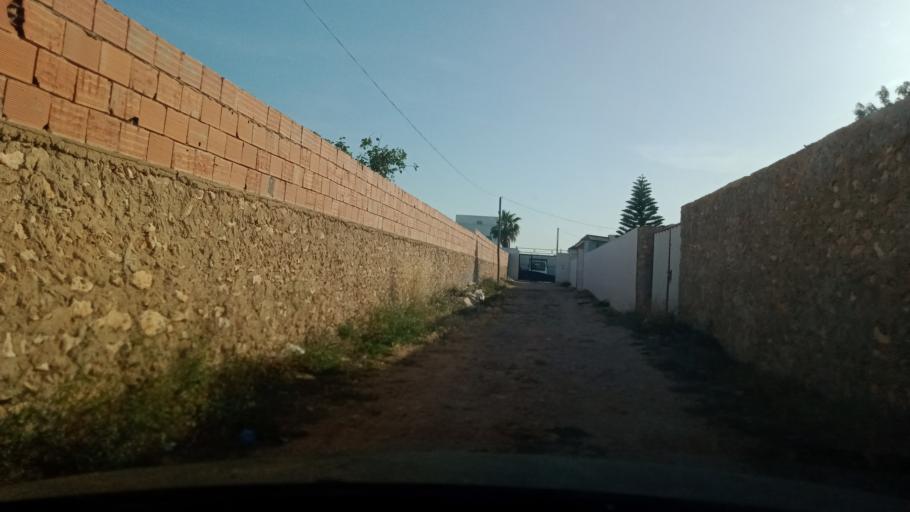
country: TN
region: Safaqis
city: Sfax
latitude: 34.8168
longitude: 10.7388
